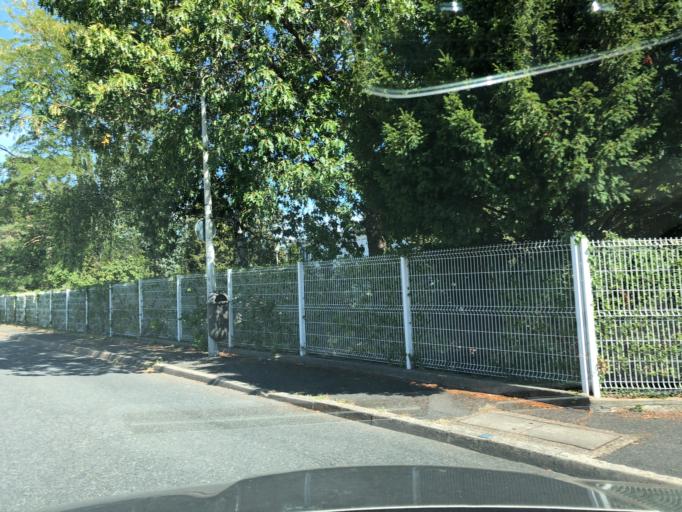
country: FR
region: Centre
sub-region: Departement d'Indre-et-Loire
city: Saint-Cyr-sur-Loire
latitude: 47.4273
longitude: 0.6882
